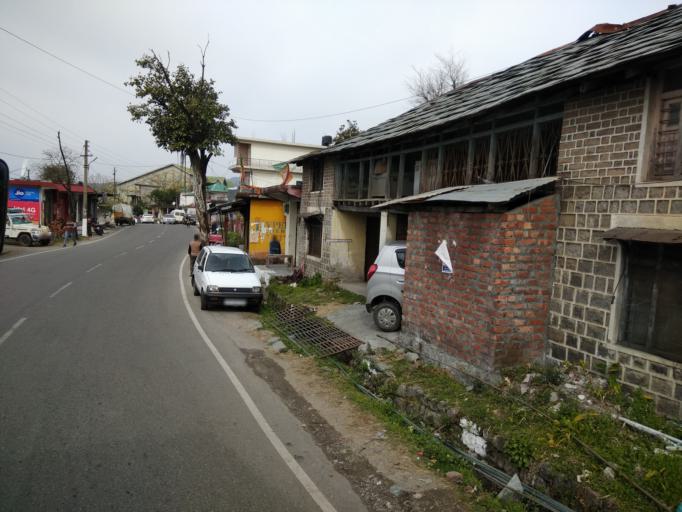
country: IN
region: Himachal Pradesh
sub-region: Kangra
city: Dharmsala
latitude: 32.1899
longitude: 76.3545
